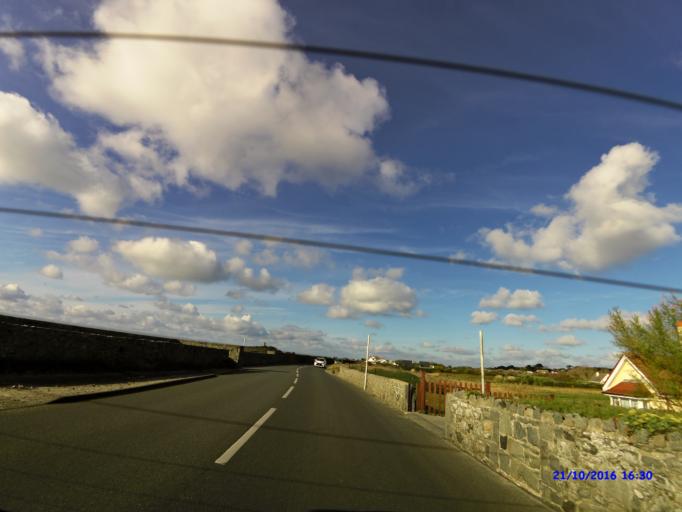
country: GG
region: St Peter Port
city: Saint Peter Port
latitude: 49.4466
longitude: -2.6492
